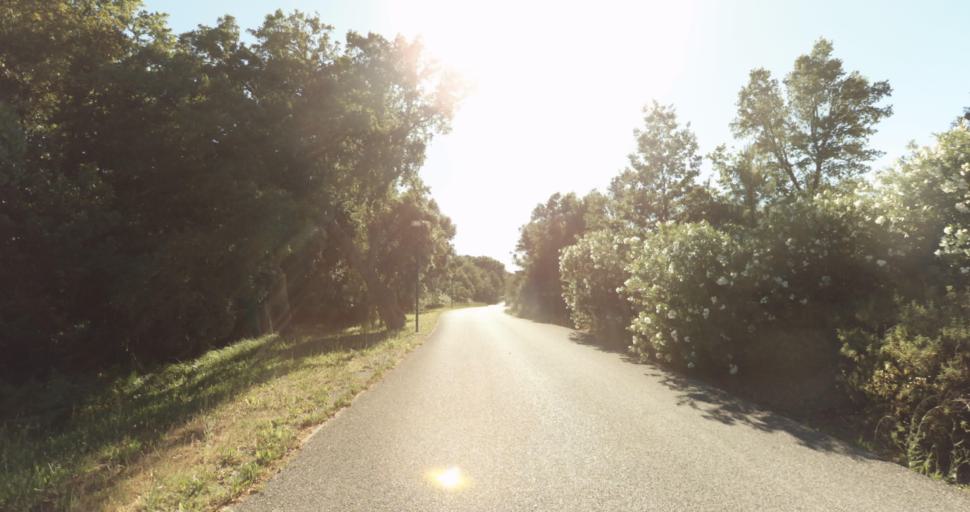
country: FR
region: Provence-Alpes-Cote d'Azur
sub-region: Departement du Var
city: Gassin
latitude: 43.2519
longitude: 6.6040
